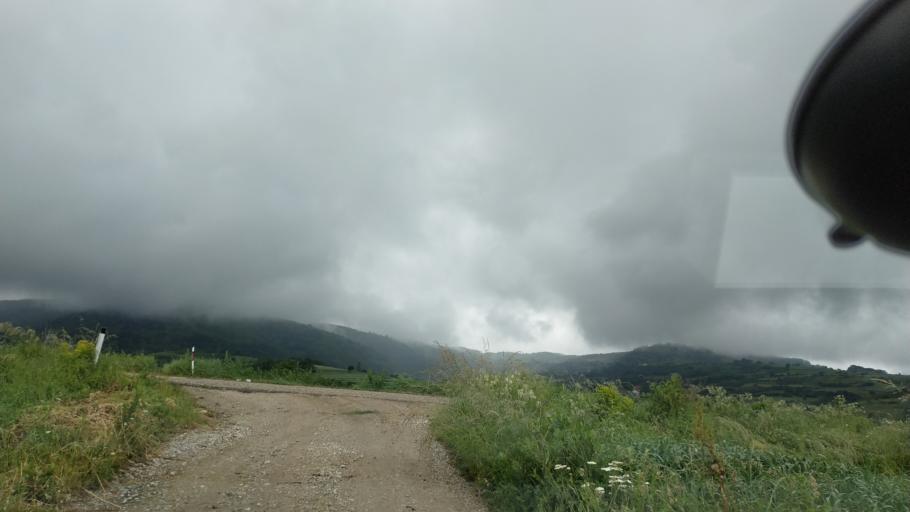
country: RS
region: Central Serbia
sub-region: Toplicki Okrug
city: Prokuplje
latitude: 43.3939
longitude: 21.5708
